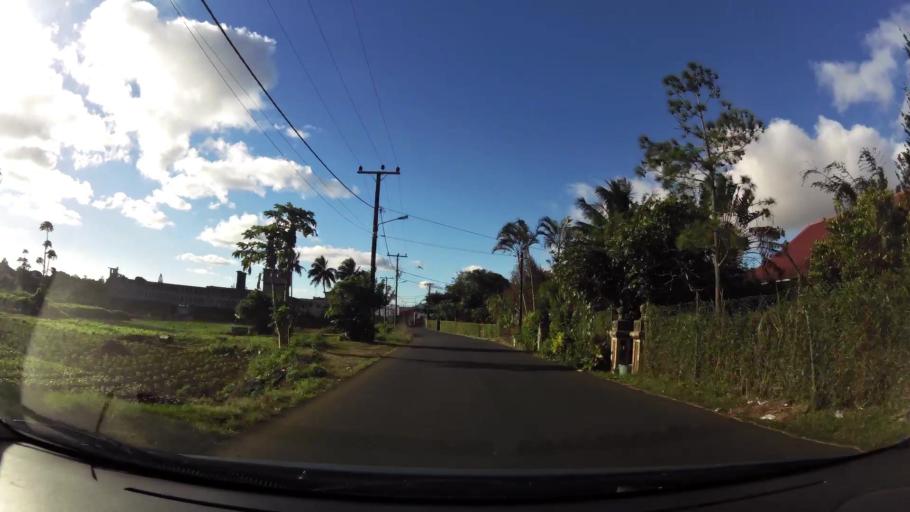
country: MU
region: Plaines Wilhems
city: Vacoas
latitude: -20.2888
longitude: 57.4972
